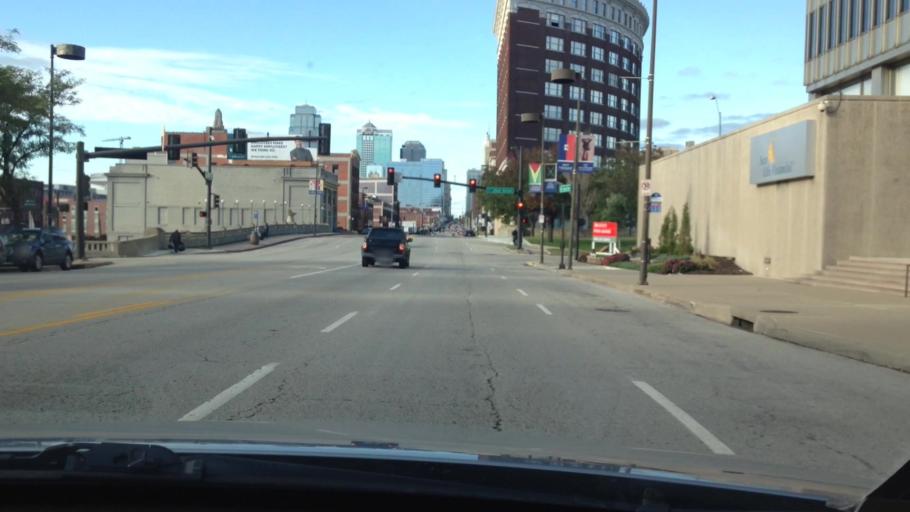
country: US
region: Missouri
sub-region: Jackson County
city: Kansas City
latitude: 39.0857
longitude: -94.5816
